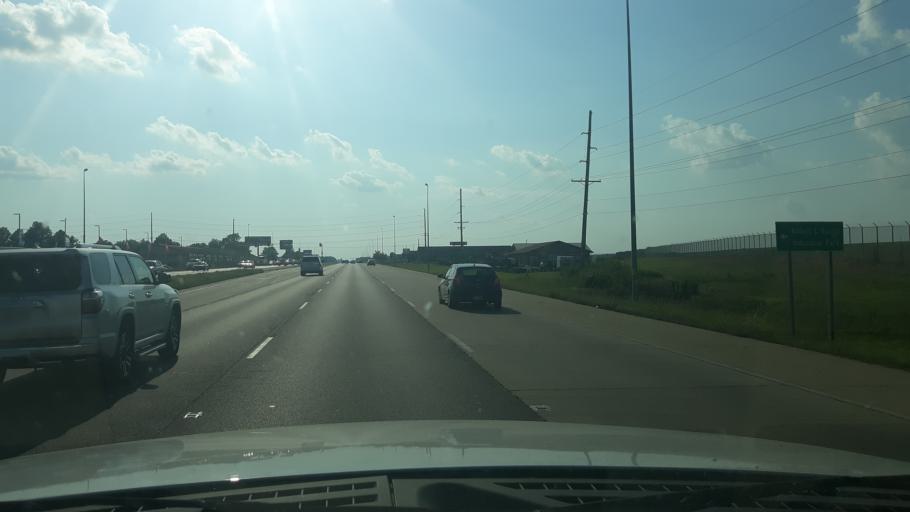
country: US
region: Illinois
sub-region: Williamson County
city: Energy
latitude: 37.7452
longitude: -88.9994
